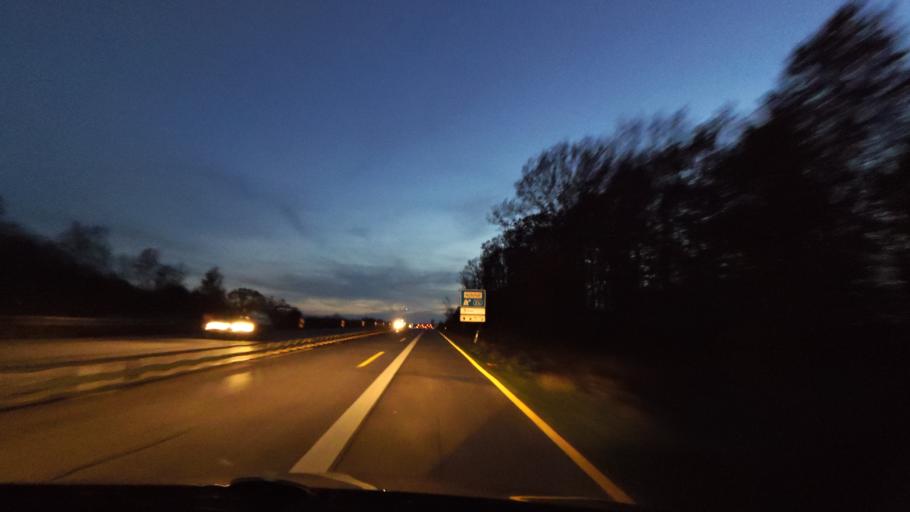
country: DE
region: Saxony-Anhalt
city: Osterfeld
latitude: 51.0601
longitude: 11.9496
